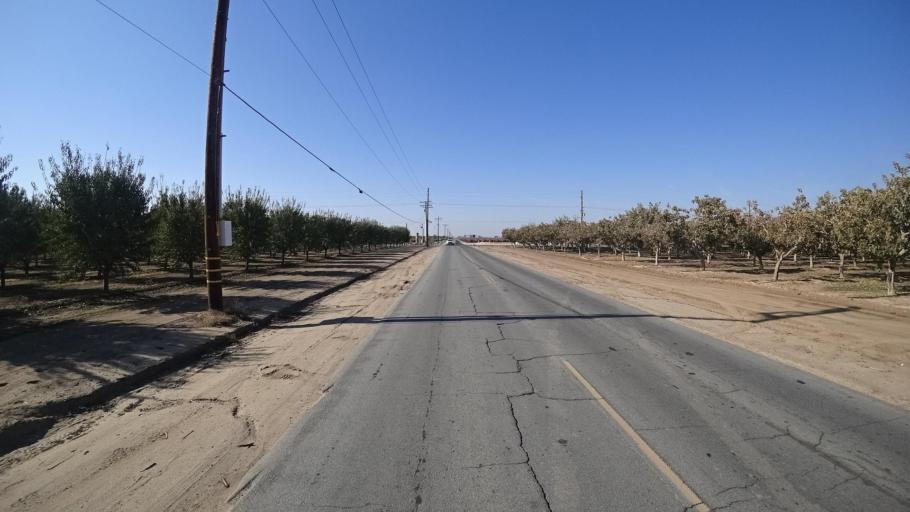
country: US
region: California
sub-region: Kern County
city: McFarland
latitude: 35.7178
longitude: -119.2039
